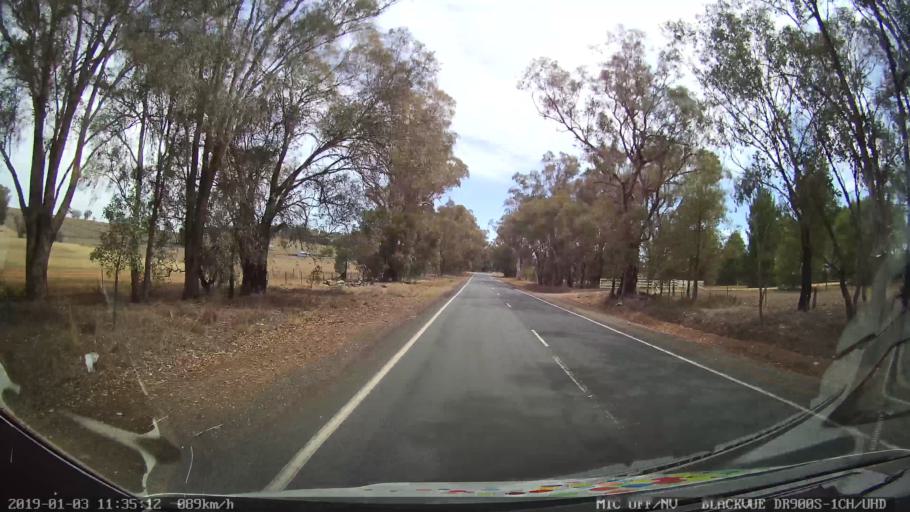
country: AU
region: New South Wales
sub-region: Weddin
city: Grenfell
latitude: -33.9253
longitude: 148.1598
